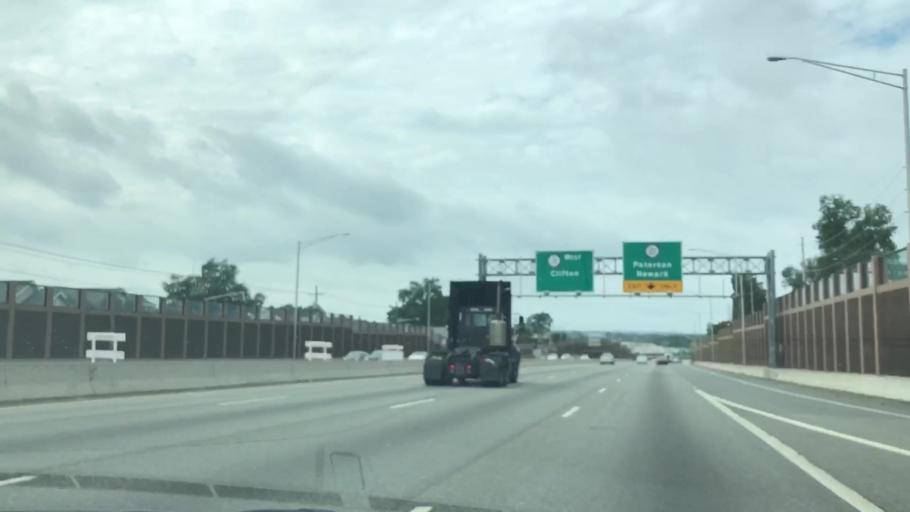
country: US
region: New Jersey
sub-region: Bergen County
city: Lyndhurst
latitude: 40.8174
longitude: -74.1146
